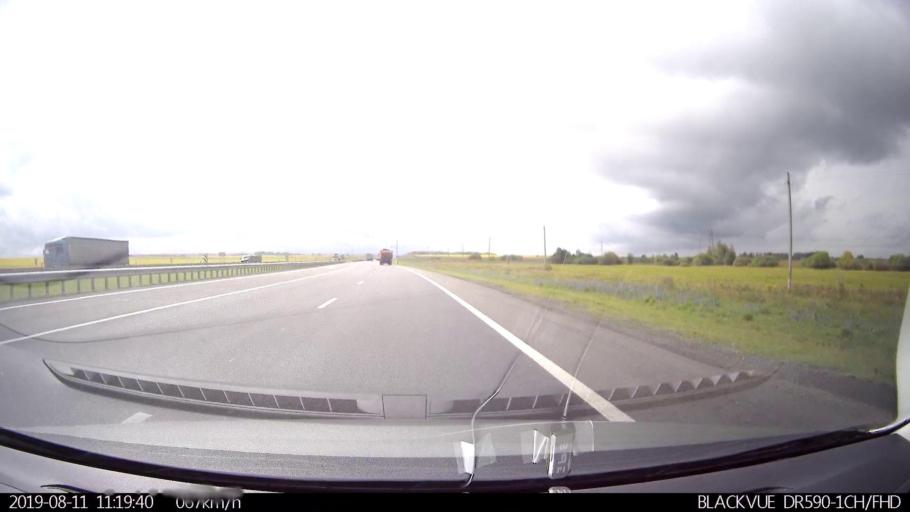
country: RU
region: Ulyanovsk
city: Novoul'yanovsk
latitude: 54.1662
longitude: 48.2646
